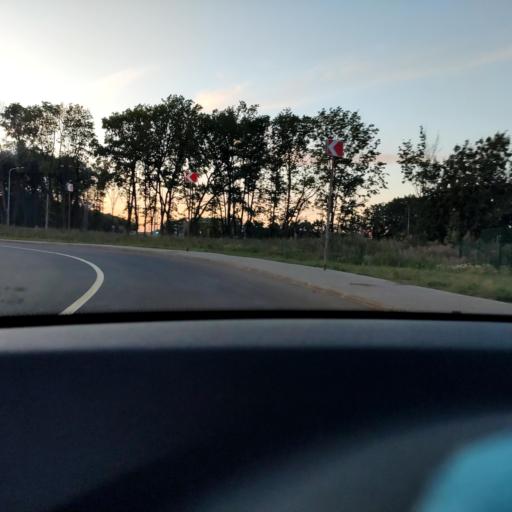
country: RU
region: Samara
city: Petra-Dubrava
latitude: 53.2782
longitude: 50.2532
